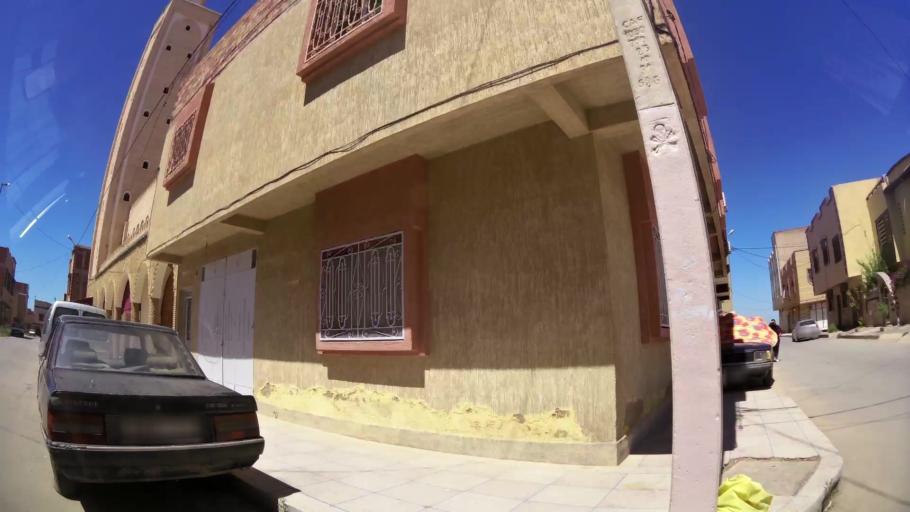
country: MA
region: Oriental
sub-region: Oujda-Angad
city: Oujda
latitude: 34.6777
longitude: -1.8680
